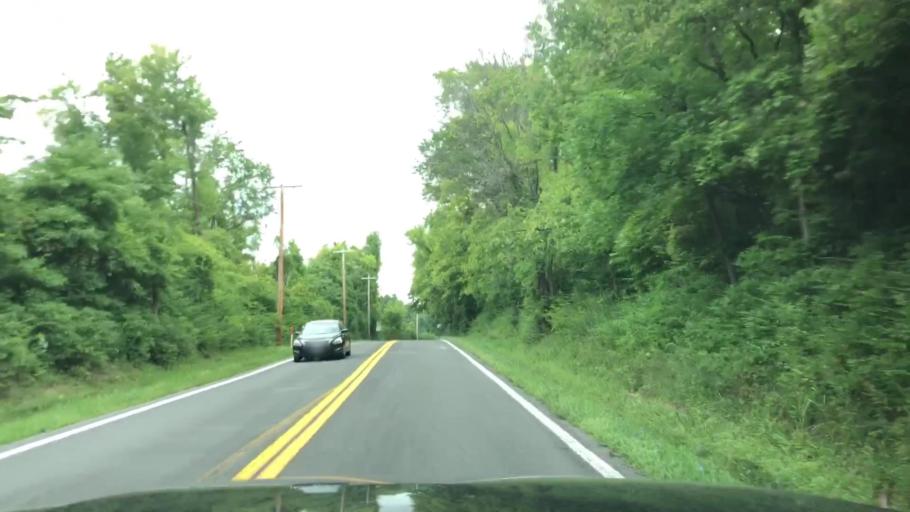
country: US
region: Missouri
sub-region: Saint Louis County
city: Hazelwood
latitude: 38.8117
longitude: -90.3791
